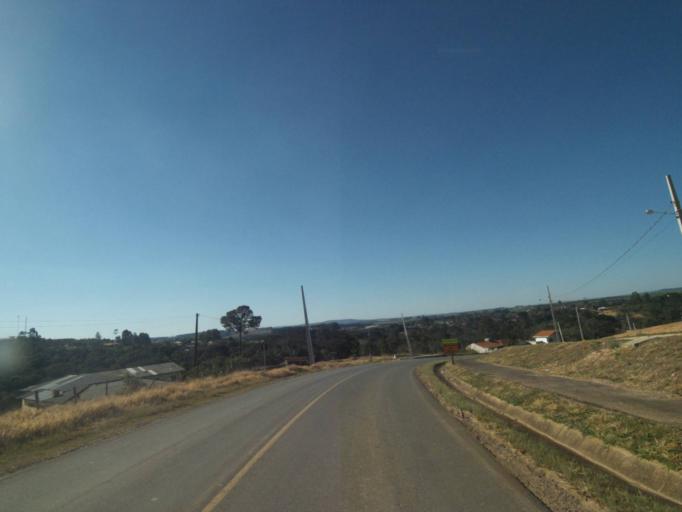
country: BR
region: Parana
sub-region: Tibagi
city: Tibagi
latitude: -24.5196
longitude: -50.4257
